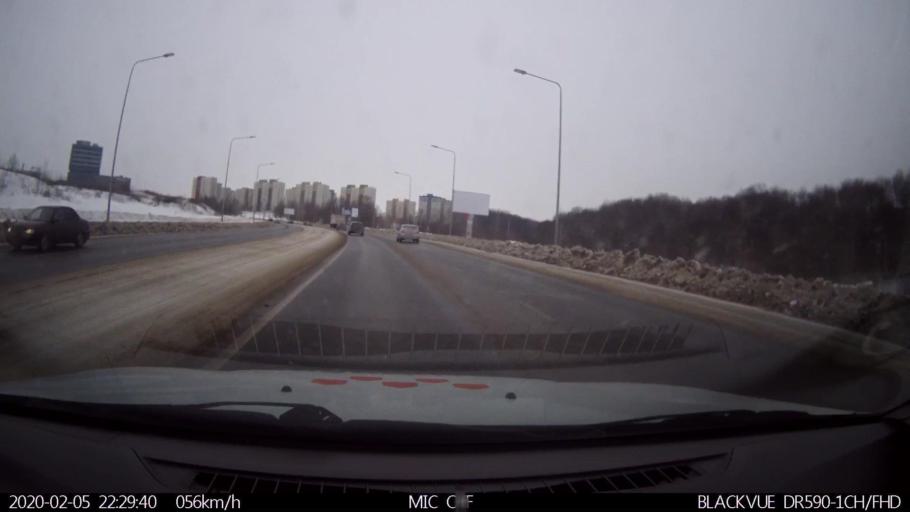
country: RU
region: Nizjnij Novgorod
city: Imeni Stepana Razina
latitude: 54.7477
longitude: 44.1473
